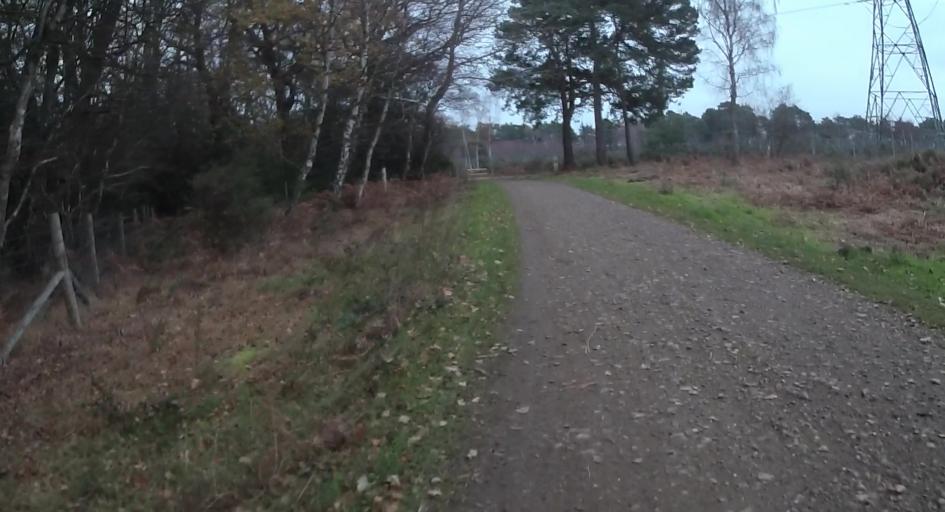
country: GB
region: England
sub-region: Surrey
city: Bagshot
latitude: 51.3432
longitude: -0.6710
